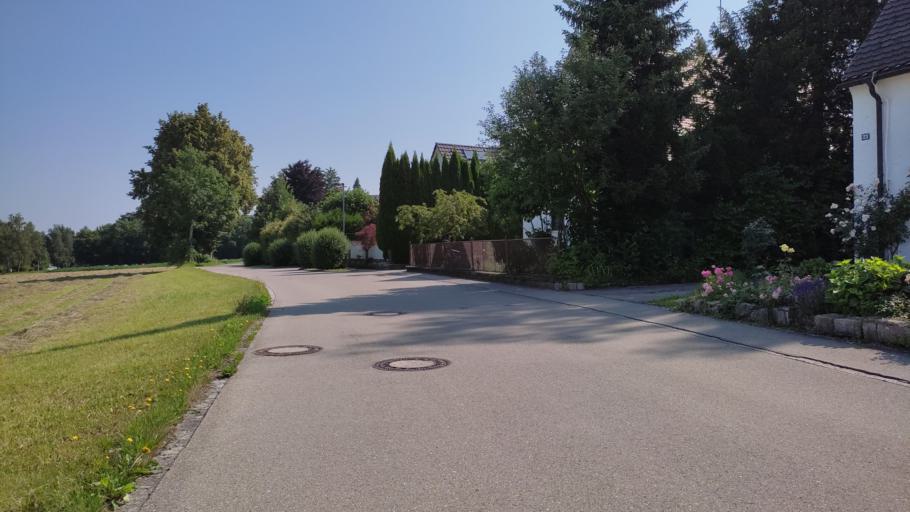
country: DE
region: Bavaria
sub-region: Swabia
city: Bad Worishofen
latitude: 47.9995
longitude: 10.5807
